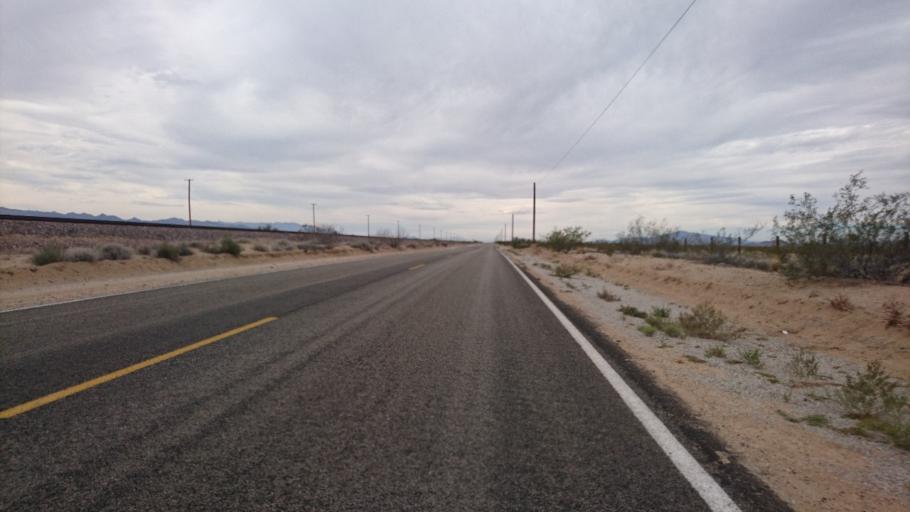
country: US
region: California
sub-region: San Bernardino County
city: Needles
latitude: 34.9065
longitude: -115.0842
